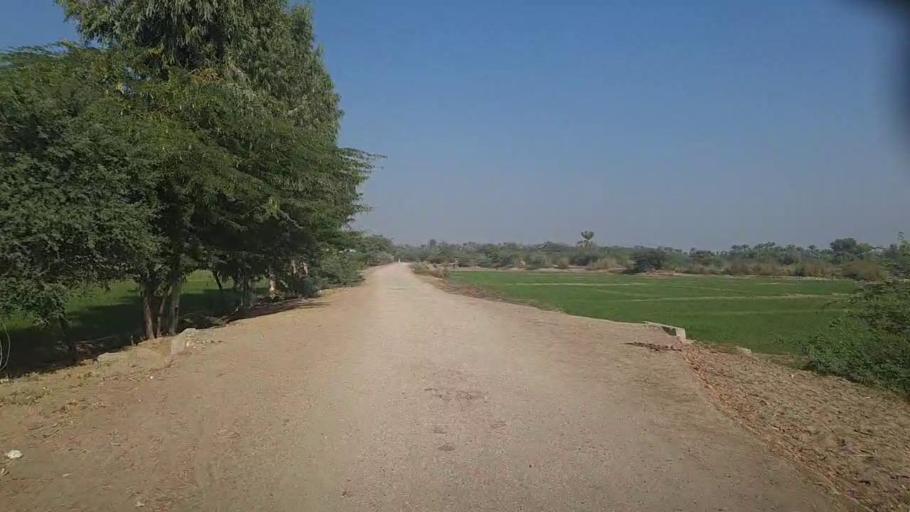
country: PK
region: Sindh
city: Kot Diji
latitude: 27.4158
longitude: 68.7054
